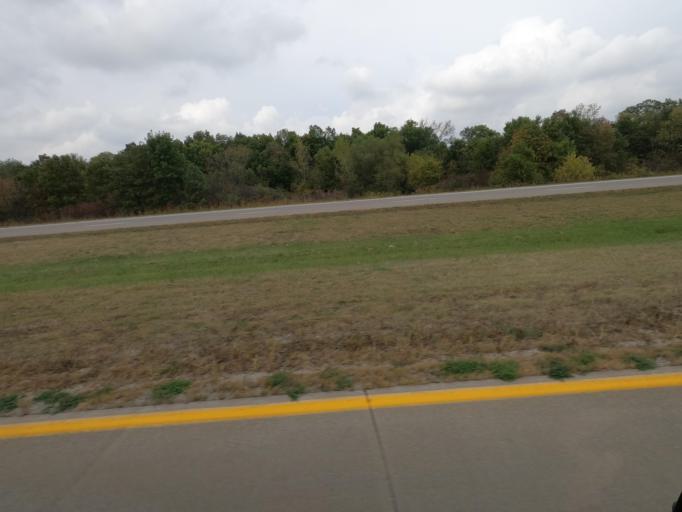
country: US
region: Iowa
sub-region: Wapello County
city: Ottumwa
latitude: 41.0962
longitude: -92.4989
